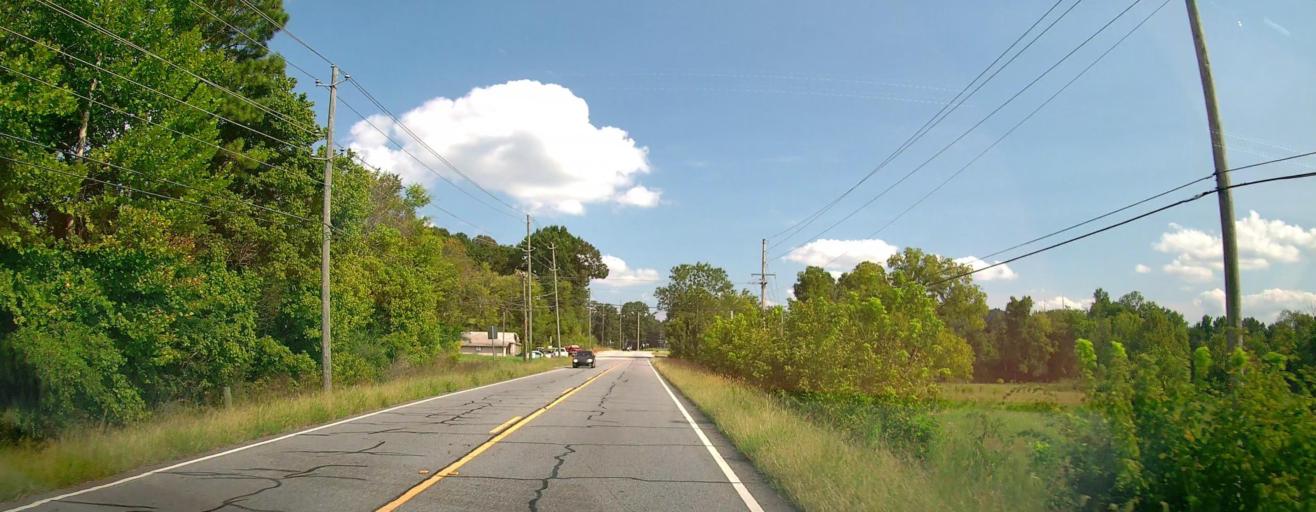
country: US
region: Georgia
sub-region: Catoosa County
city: Ringgold
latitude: 34.9080
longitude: -85.0804
